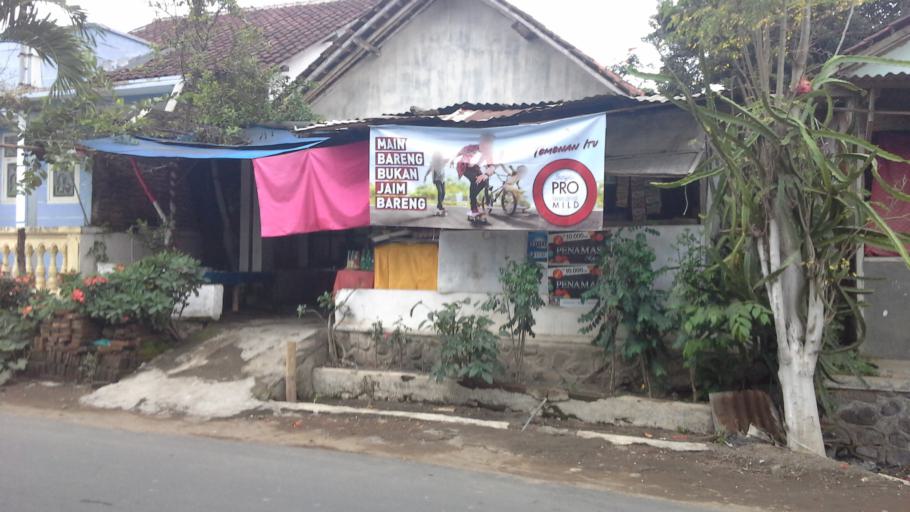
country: ID
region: East Java
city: Maesan
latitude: -8.0275
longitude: 113.7806
